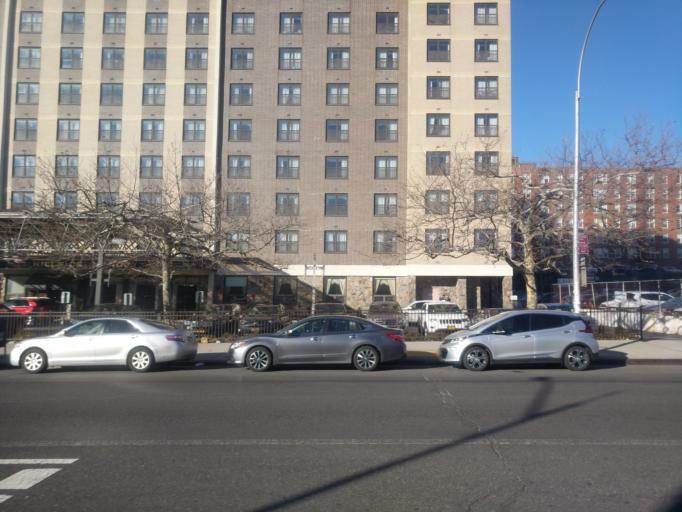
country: US
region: New York
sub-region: Queens County
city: Jamaica
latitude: 40.7138
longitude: -73.7795
